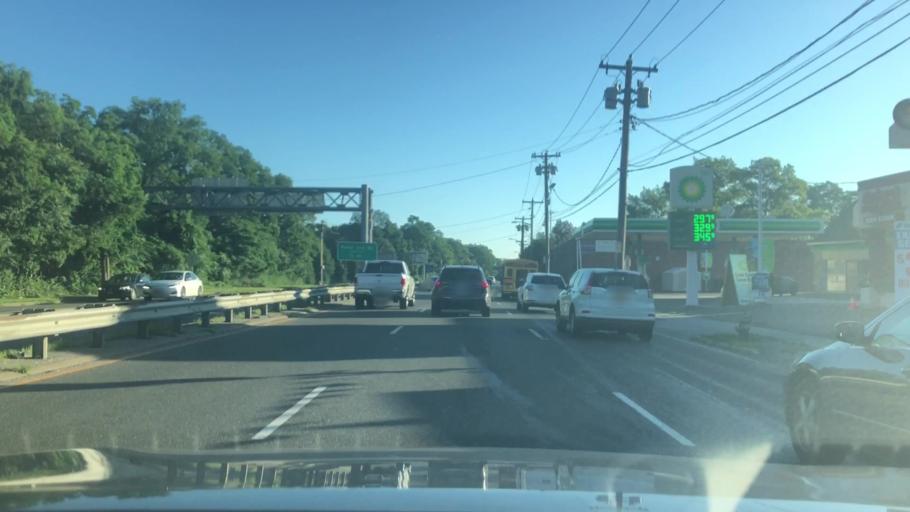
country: US
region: New York
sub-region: Nassau County
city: Hempstead
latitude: 40.6927
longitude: -73.6320
